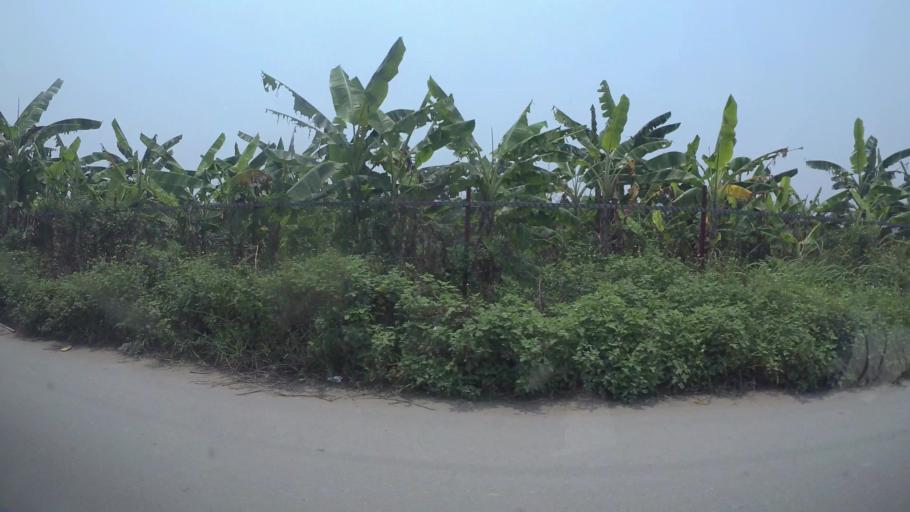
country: VN
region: Ha Noi
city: Ha Dong
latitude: 20.9979
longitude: 105.7662
